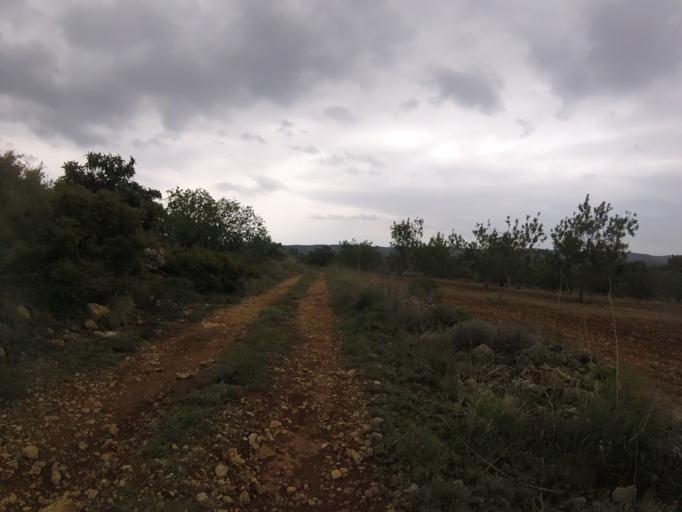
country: ES
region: Valencia
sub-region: Provincia de Castello
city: Cuevas de Vinroma
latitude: 40.2923
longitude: 0.0893
